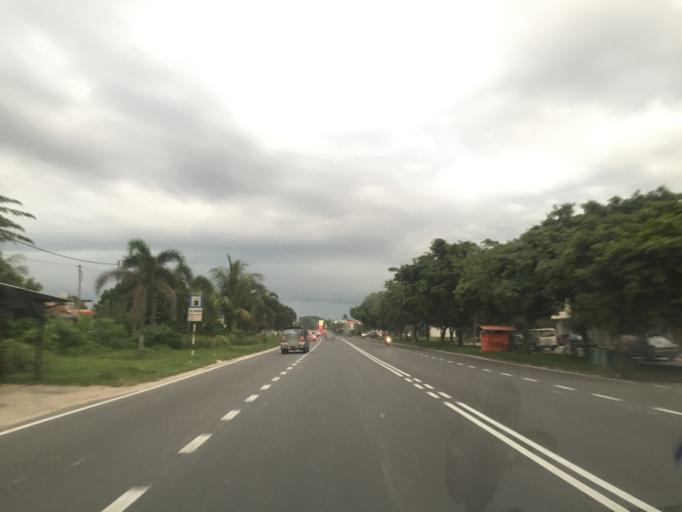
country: MY
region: Penang
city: Tasek Glugor
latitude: 5.5151
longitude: 100.5419
